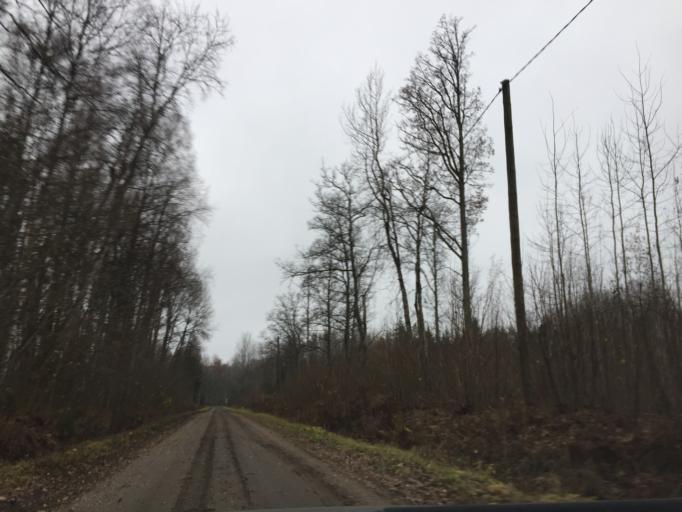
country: LV
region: Limbazu Rajons
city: Limbazi
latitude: 57.4970
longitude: 24.7700
